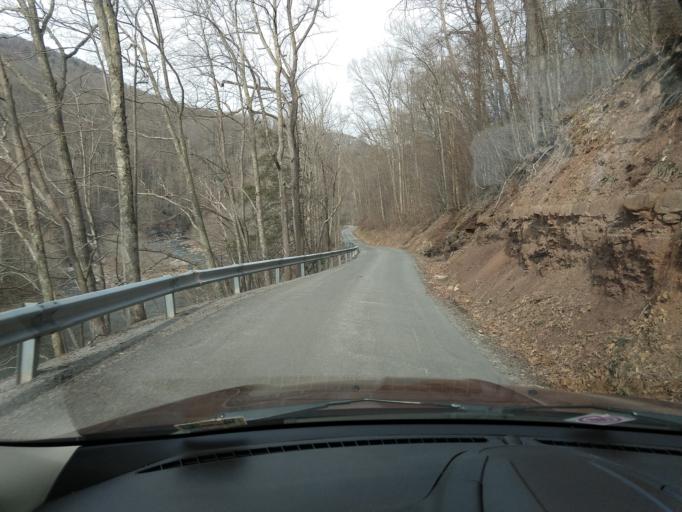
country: US
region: West Virginia
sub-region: Tucker County
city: Parsons
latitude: 39.0322
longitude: -79.5899
